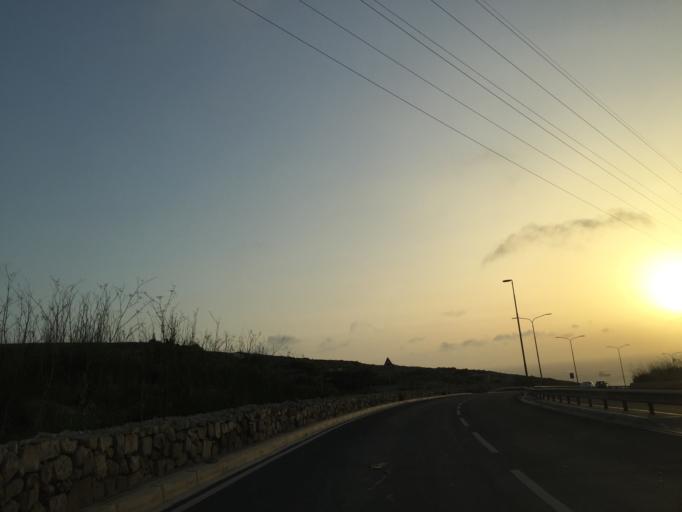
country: MT
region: Il-Mellieha
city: Mellieha
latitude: 35.9550
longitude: 14.3557
